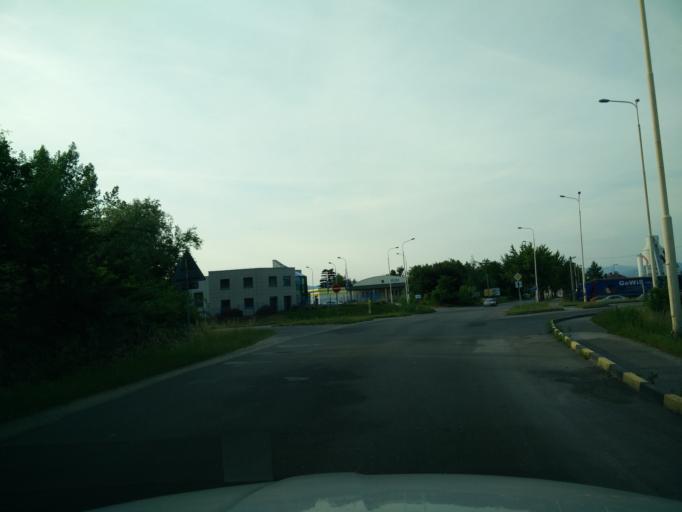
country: SK
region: Nitriansky
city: Prievidza
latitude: 48.7590
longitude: 18.6173
